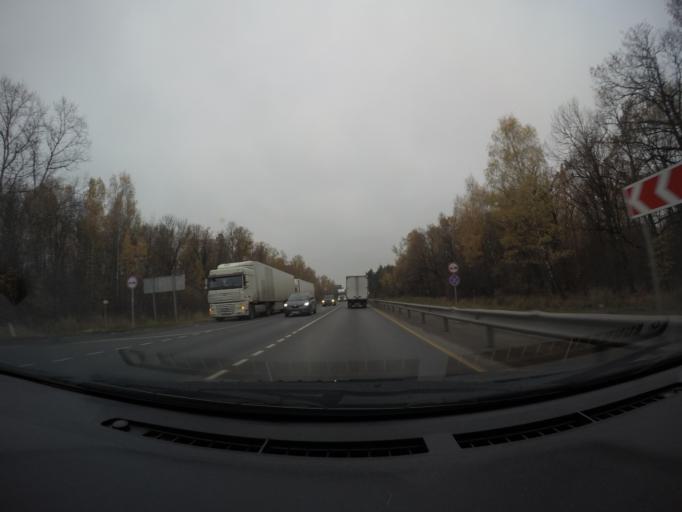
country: RU
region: Moskovskaya
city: Bronnitsy
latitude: 55.4045
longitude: 38.2289
